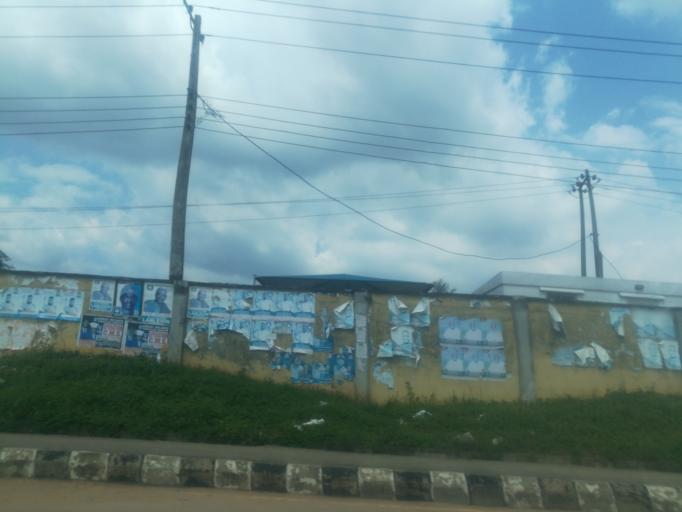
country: NG
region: Oyo
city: Ibadan
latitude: 7.4157
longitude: 3.8626
